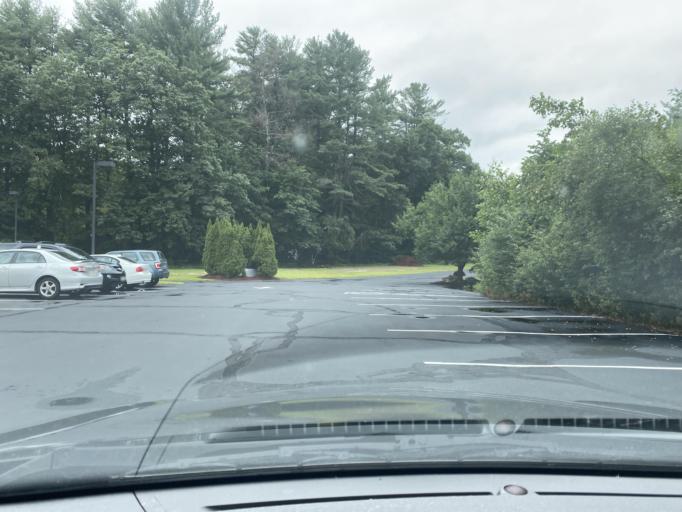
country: US
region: New Hampshire
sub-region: Rockingham County
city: Windham
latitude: 42.8067
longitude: -71.2741
